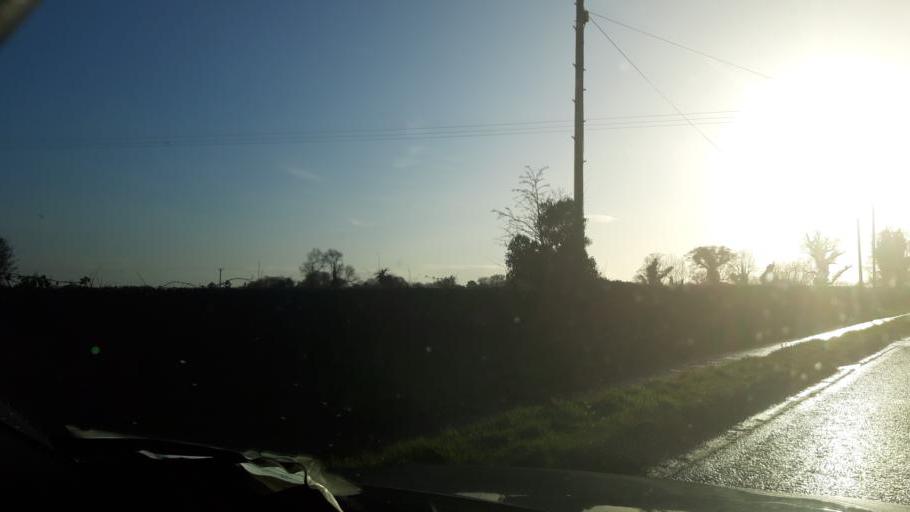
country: GB
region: Northern Ireland
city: Garvagh
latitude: 54.9925
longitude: -6.6826
